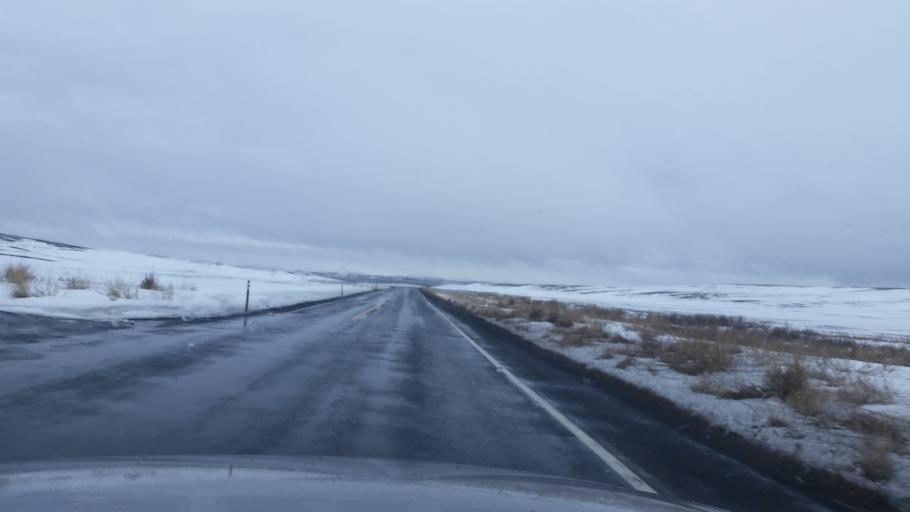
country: US
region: Washington
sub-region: Lincoln County
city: Davenport
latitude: 47.3848
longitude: -118.1379
